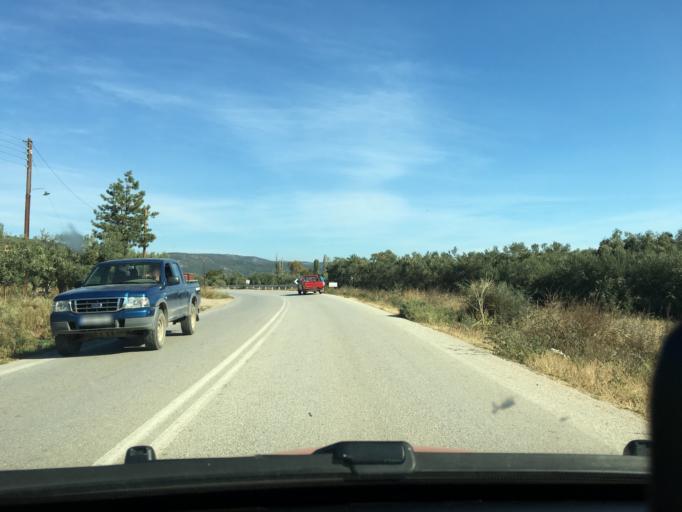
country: GR
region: Central Macedonia
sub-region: Nomos Chalkidikis
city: Ormylia
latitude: 40.2794
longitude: 23.5425
